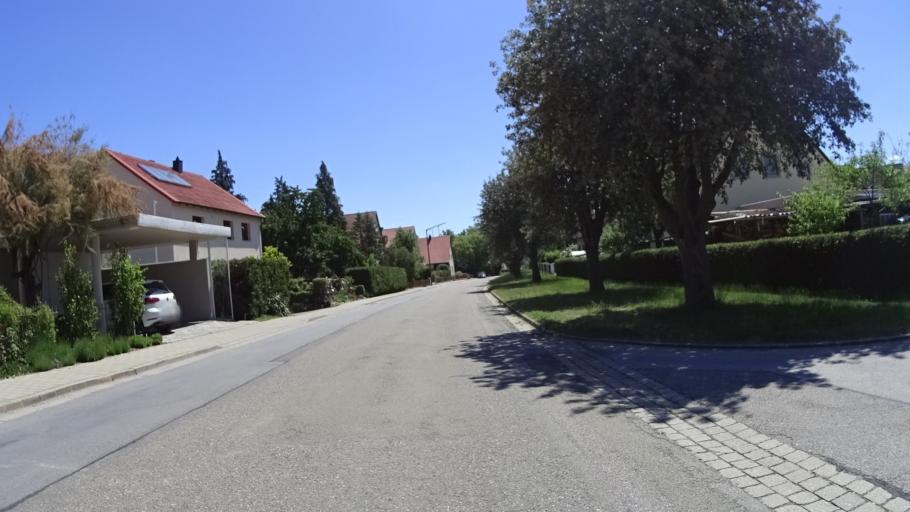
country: DE
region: Bavaria
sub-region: Regierungsbezirk Mittelfranken
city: Hottingen
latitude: 49.0778
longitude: 11.0191
